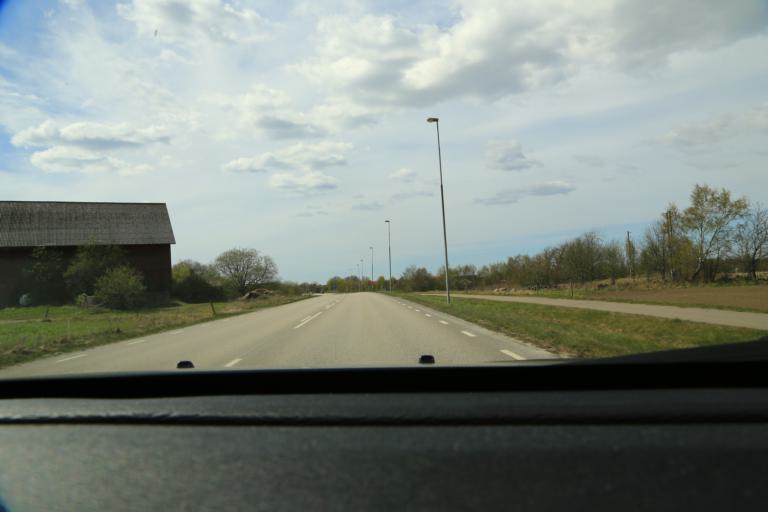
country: SE
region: Halland
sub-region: Varbergs Kommun
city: Traslovslage
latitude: 57.1100
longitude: 12.3044
